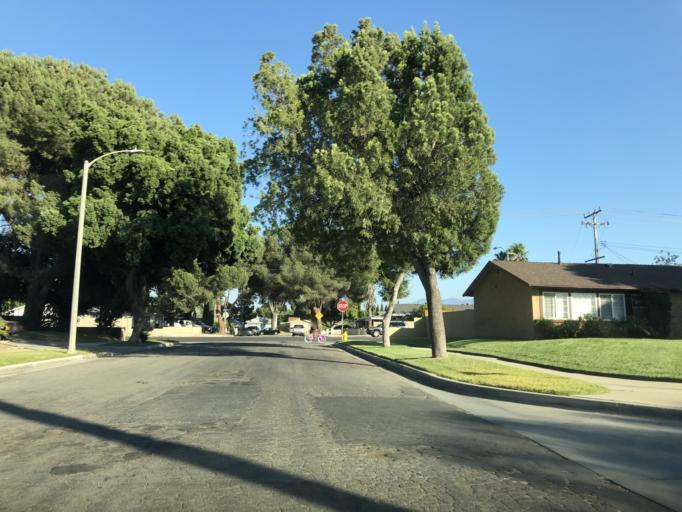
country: US
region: California
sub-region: Riverside County
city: Corona
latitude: 33.9013
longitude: -117.5729
